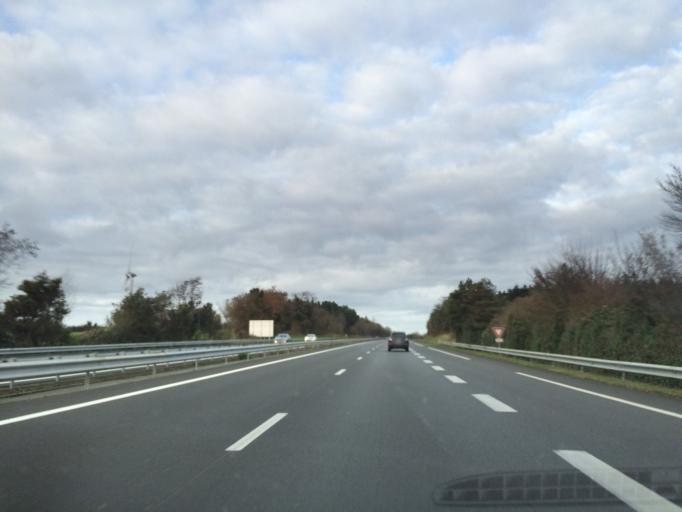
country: FR
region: Poitou-Charentes
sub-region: Departement de la Charente-Maritime
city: Saint-Jean-d'Angely
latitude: 46.0155
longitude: -0.5414
